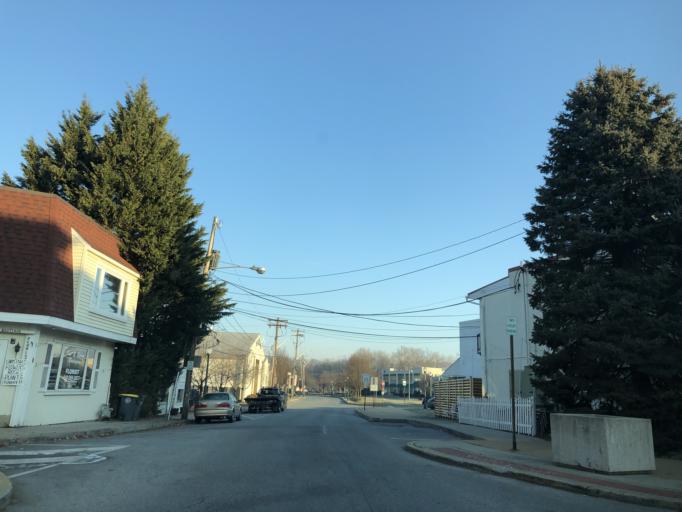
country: US
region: Pennsylvania
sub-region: Chester County
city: Downingtown
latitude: 40.0068
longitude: -75.7032
